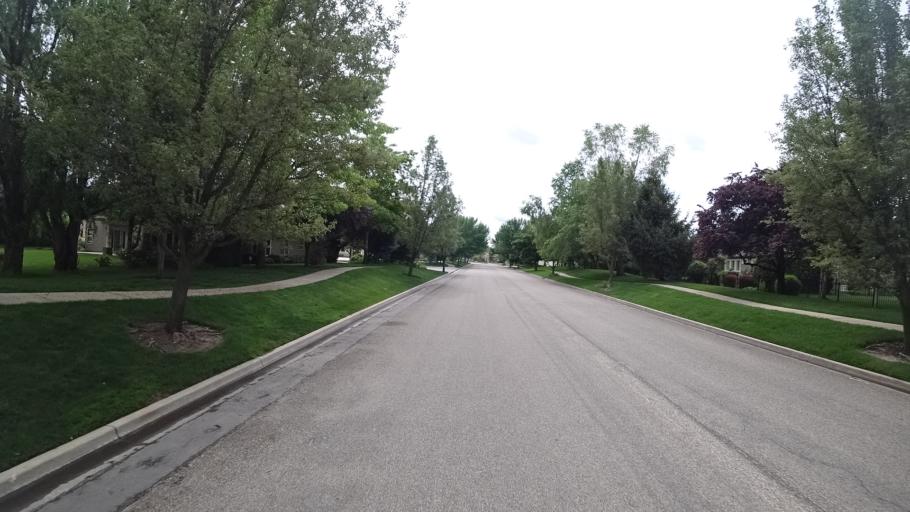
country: US
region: Idaho
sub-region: Ada County
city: Eagle
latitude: 43.6788
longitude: -116.3388
